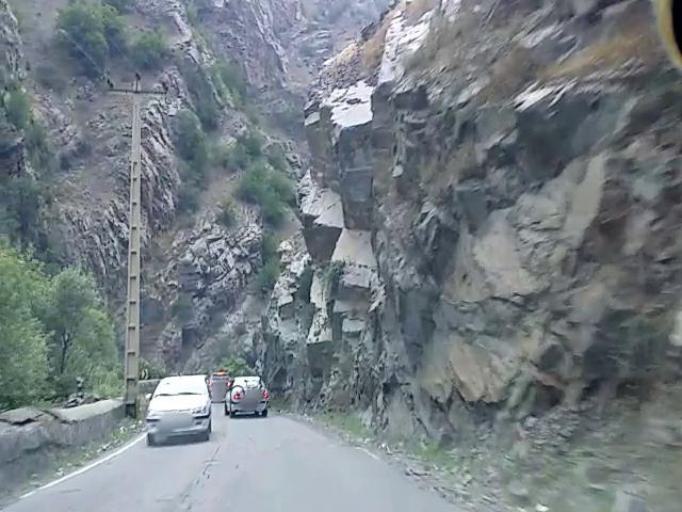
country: IR
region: Mazandaran
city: Chalus
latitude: 36.2789
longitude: 51.2433
